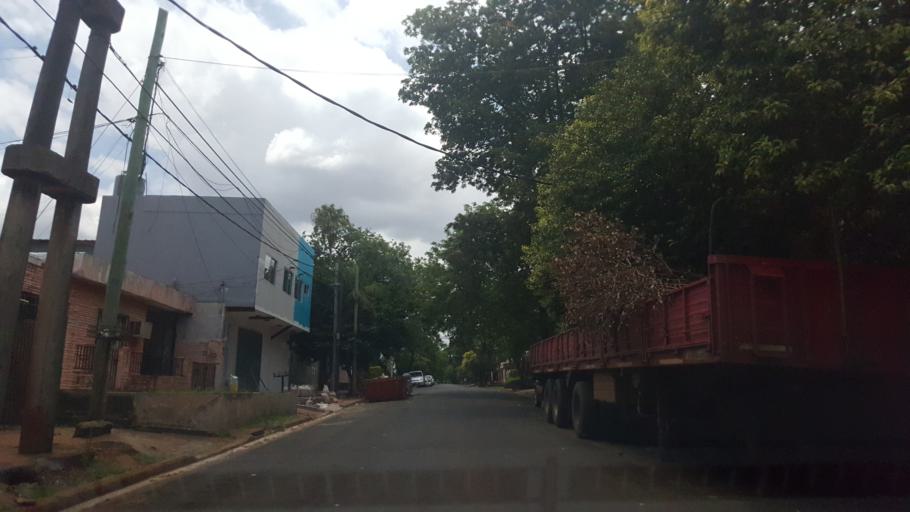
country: AR
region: Misiones
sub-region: Departamento de Capital
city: Posadas
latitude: -27.3838
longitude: -55.8959
